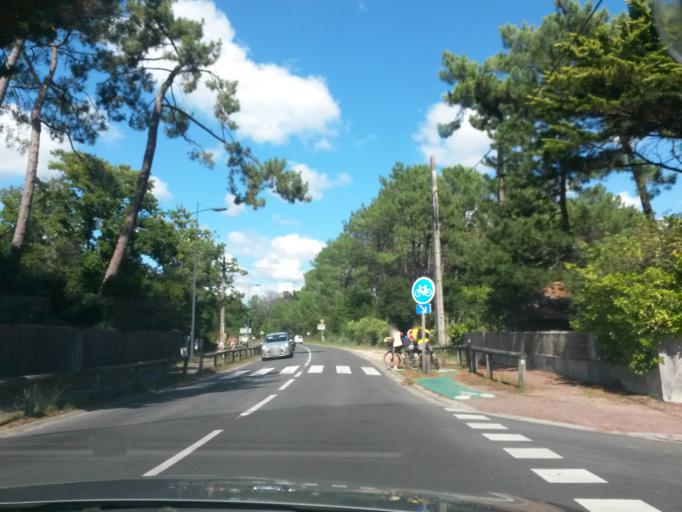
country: FR
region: Aquitaine
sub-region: Departement de la Gironde
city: Ares
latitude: 44.7283
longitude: -1.1974
